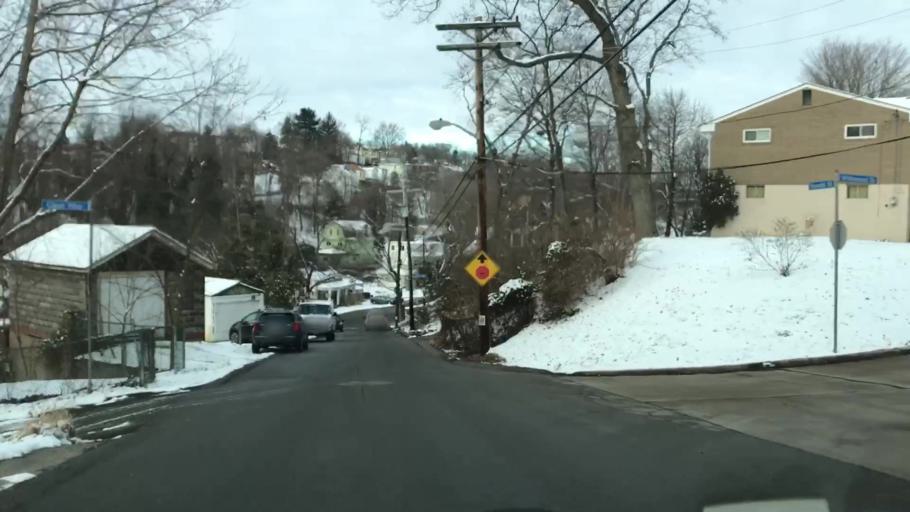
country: US
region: Pennsylvania
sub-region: Allegheny County
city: Crafton
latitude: 40.4400
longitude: -80.0495
